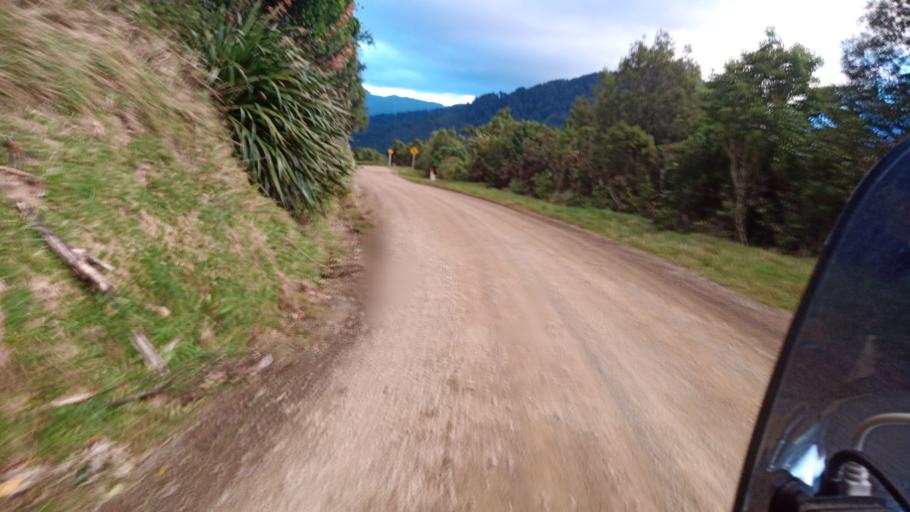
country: NZ
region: Hawke's Bay
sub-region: Wairoa District
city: Wairoa
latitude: -38.7268
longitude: 177.0657
